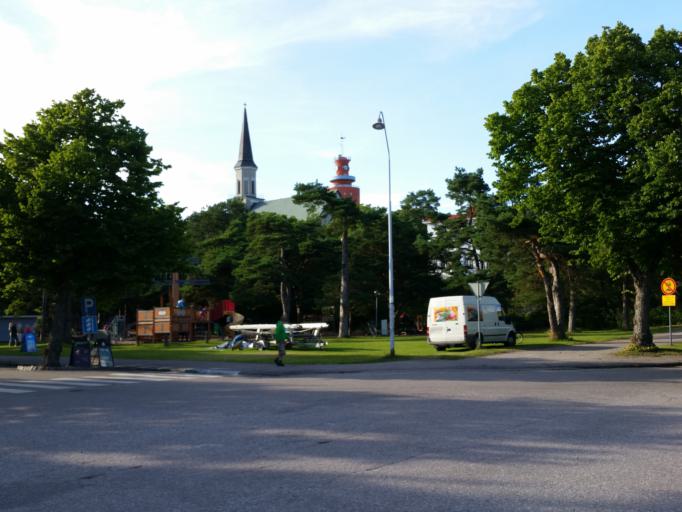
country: FI
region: Uusimaa
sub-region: Raaseporin
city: Hanko
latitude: 59.8226
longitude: 22.9719
